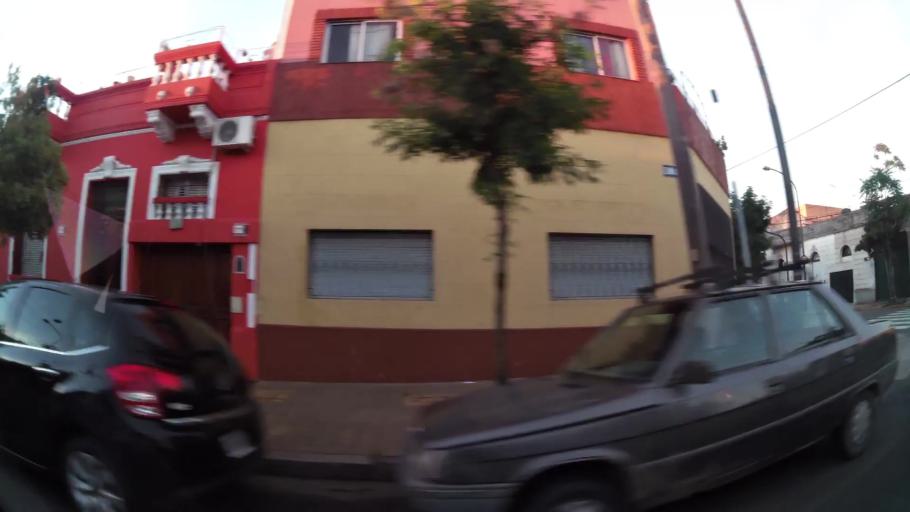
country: AR
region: Buenos Aires F.D.
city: Villa Santa Rita
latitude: -34.6392
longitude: -58.4306
